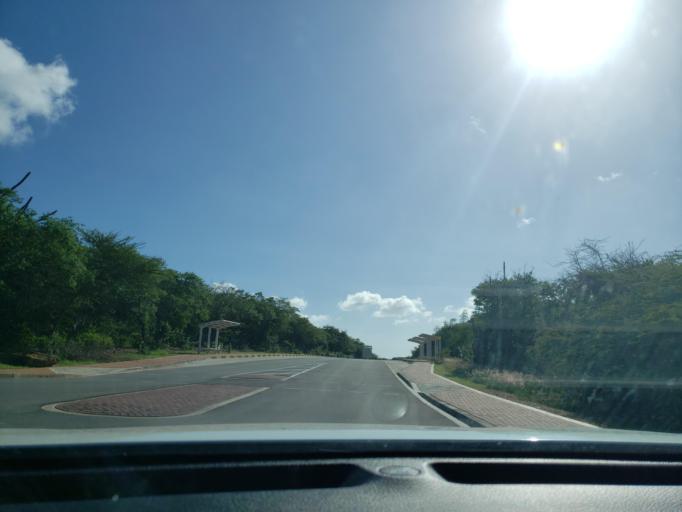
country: CW
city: Dorp Soto
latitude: 12.3508
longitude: -69.1518
